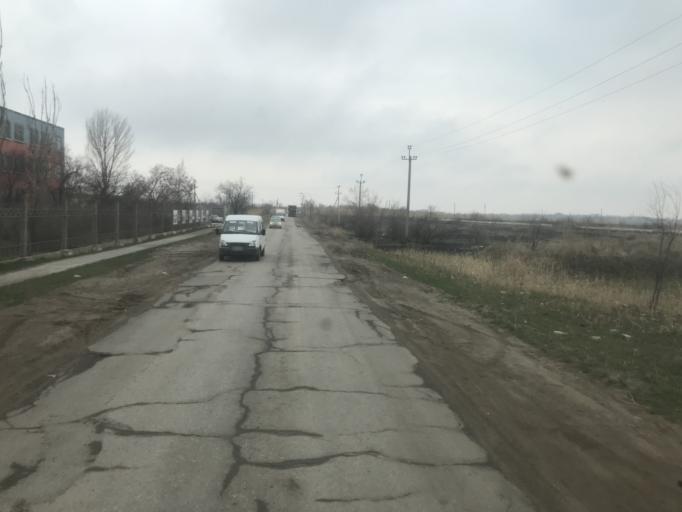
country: RU
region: Volgograd
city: Svetlyy Yar
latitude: 48.5264
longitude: 44.6142
